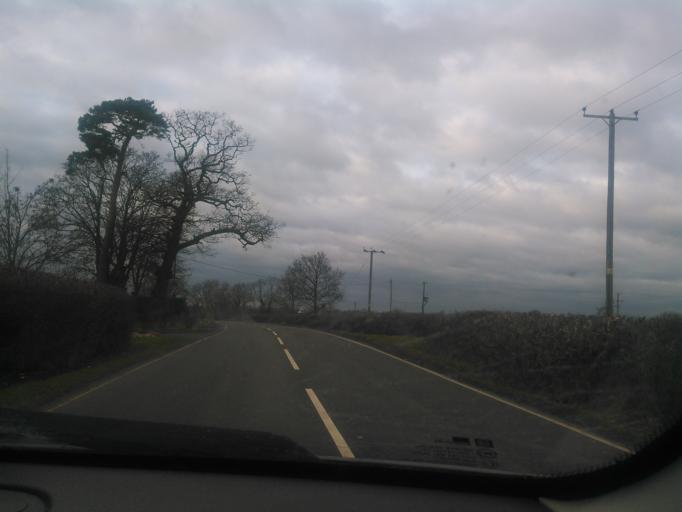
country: GB
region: England
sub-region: Leicestershire
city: Wigston Magna
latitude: 52.5740
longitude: -1.0789
